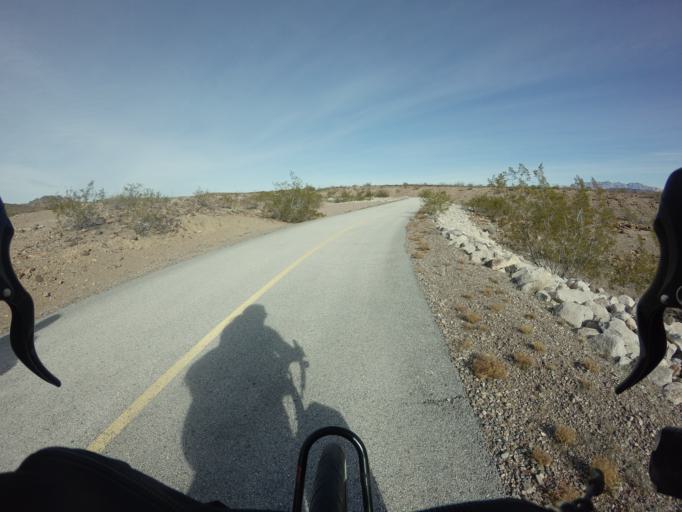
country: US
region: Nevada
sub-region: Clark County
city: Boulder City
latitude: 36.0747
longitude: -114.8126
